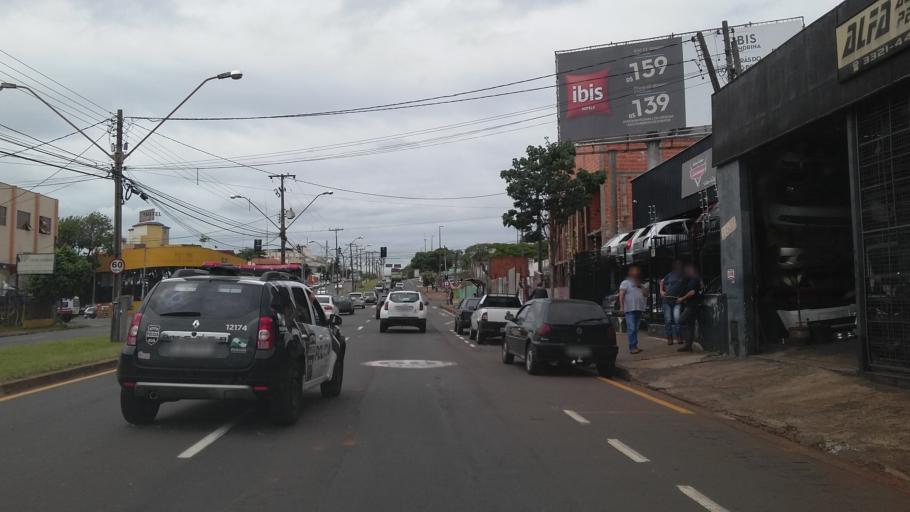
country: BR
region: Parana
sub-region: Londrina
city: Londrina
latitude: -23.3070
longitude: -51.1480
